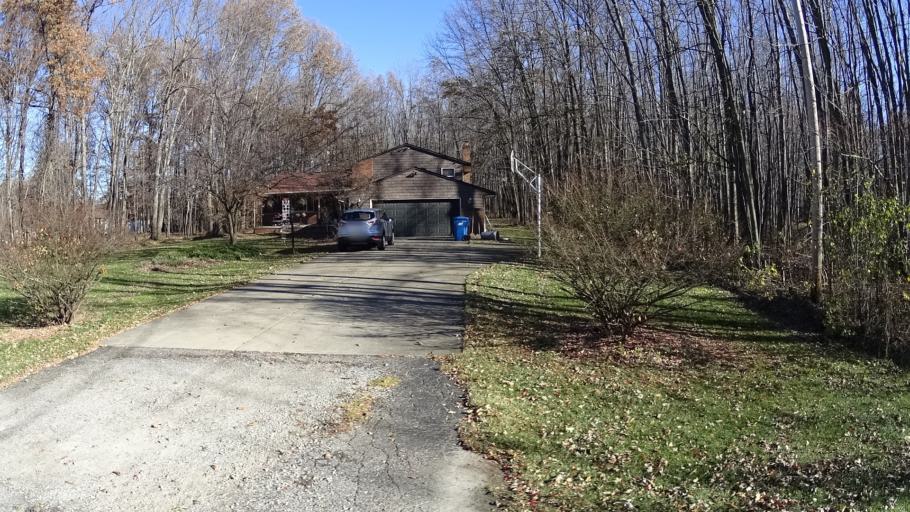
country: US
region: Ohio
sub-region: Lorain County
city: Avon Center
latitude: 41.4331
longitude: -81.9786
